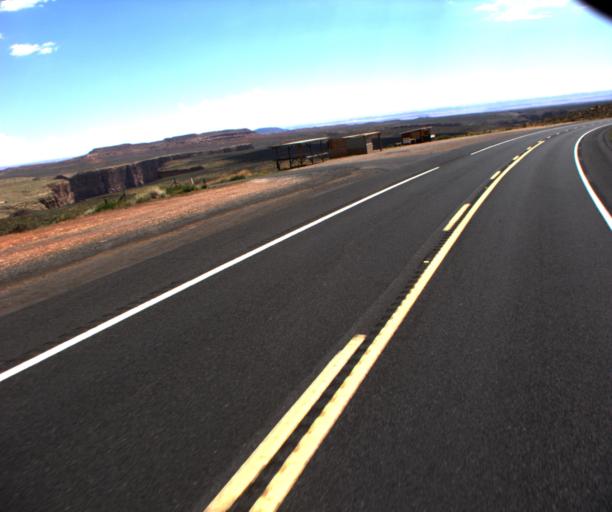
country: US
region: Arizona
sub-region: Coconino County
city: Tuba City
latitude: 35.9352
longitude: -111.6456
